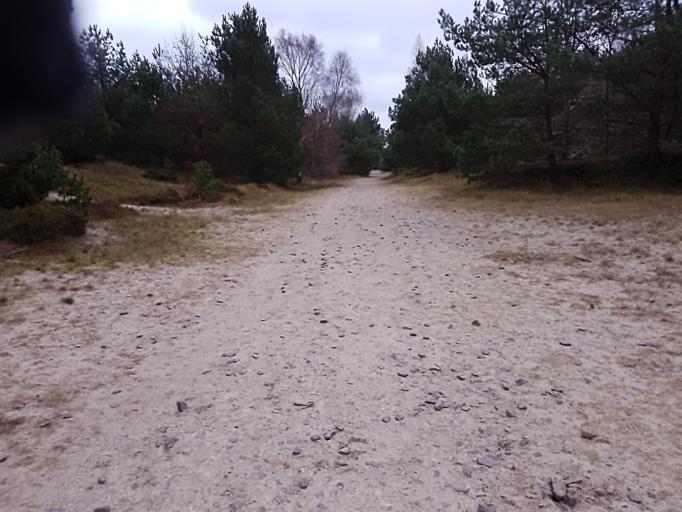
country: DE
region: Mecklenburg-Vorpommern
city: Ostseebad Binz
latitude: 54.4425
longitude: 13.5741
